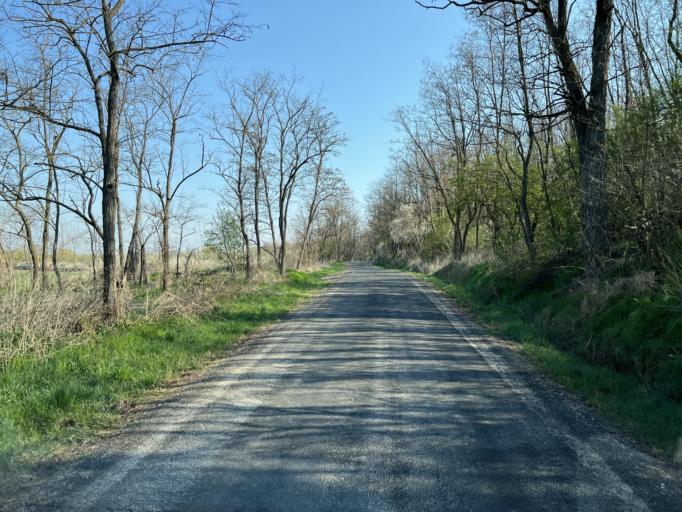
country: SK
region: Nitriansky
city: Sahy
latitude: 48.0209
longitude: 18.8255
